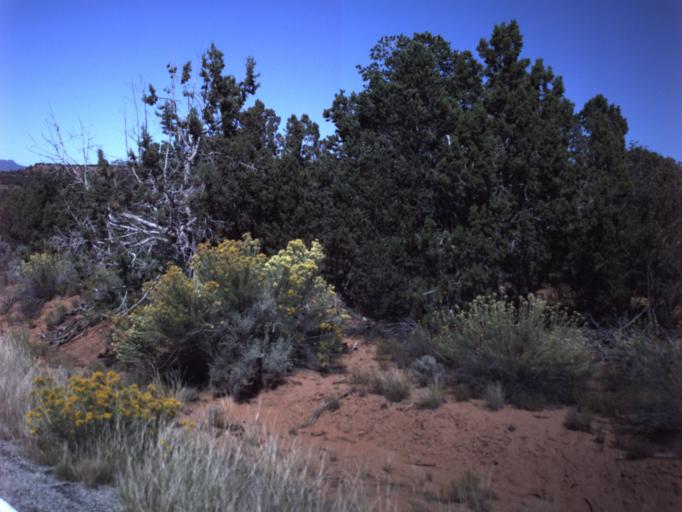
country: US
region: Utah
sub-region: San Juan County
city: Blanding
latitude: 37.3903
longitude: -109.9432
